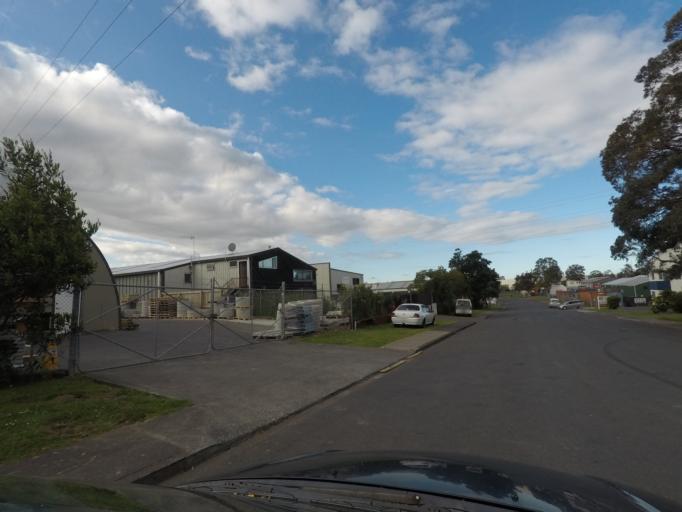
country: NZ
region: Auckland
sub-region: Auckland
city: Rosebank
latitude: -36.8885
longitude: 174.6629
